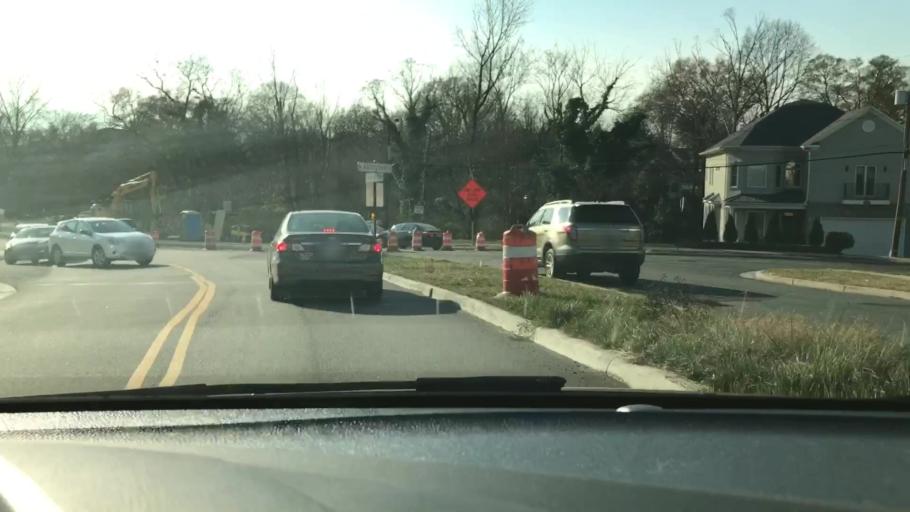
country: US
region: Virginia
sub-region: Arlington County
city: Arlington
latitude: 38.8757
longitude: -77.1158
